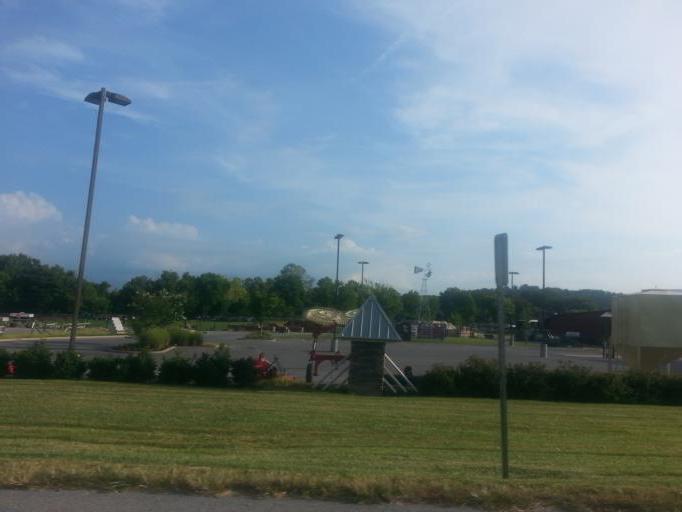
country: US
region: Tennessee
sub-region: Sevier County
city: Sevierville
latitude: 35.8702
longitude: -83.5710
